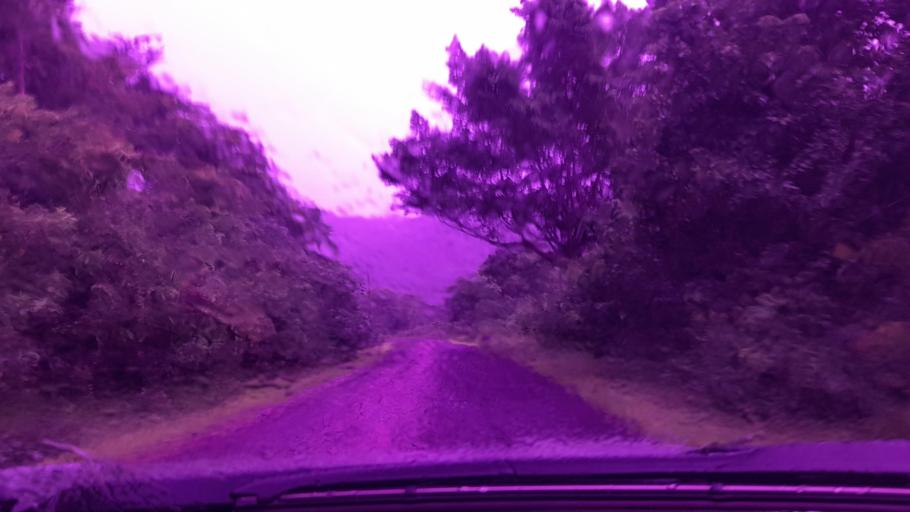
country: ET
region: Oromiya
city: Metu
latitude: 8.4786
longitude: 35.6422
